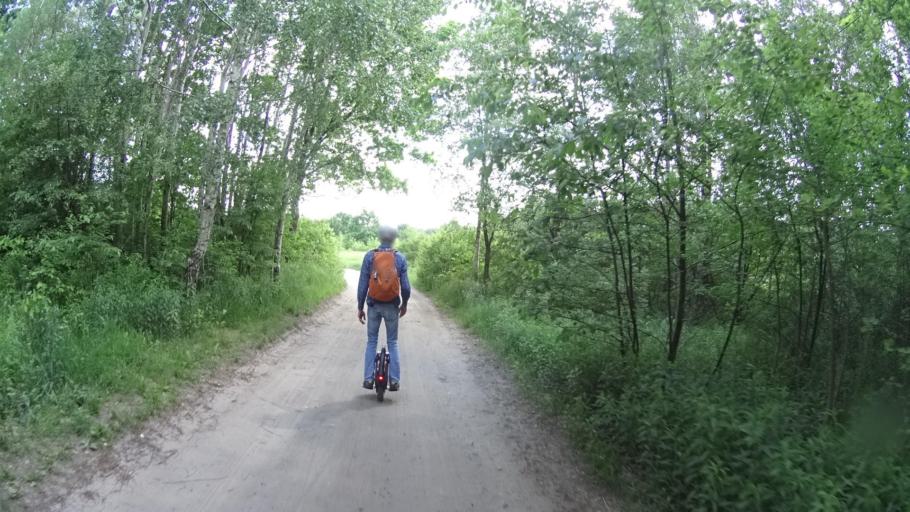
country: PL
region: Masovian Voivodeship
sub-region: Powiat piaseczynski
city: Konstancin-Jeziorna
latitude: 52.0973
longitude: 21.1039
